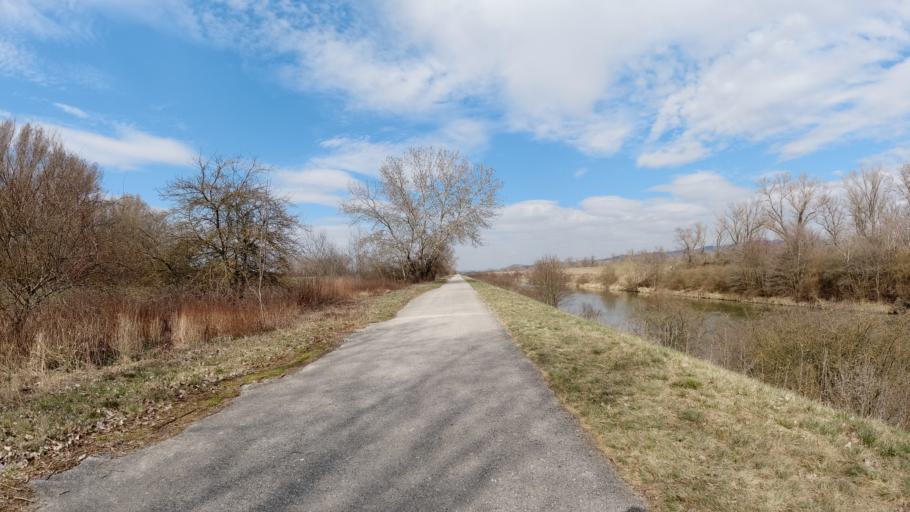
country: SK
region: Trnavsky
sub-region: Okres Trnava
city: Piestany
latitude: 48.6281
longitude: 17.8409
